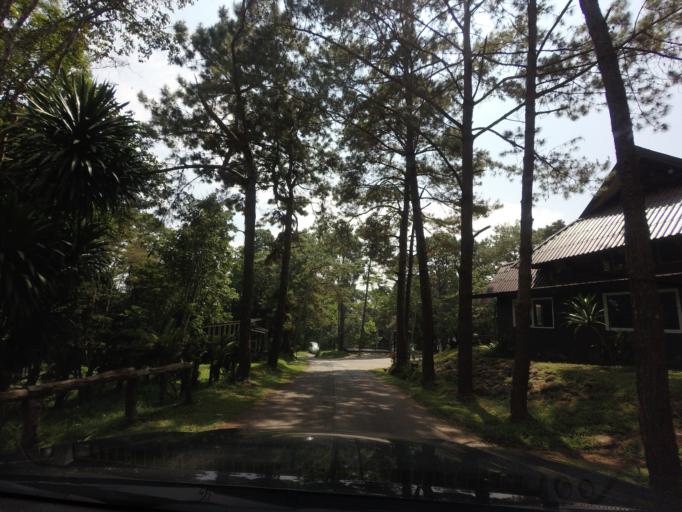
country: TH
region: Loei
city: Phu Ruea
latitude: 17.4817
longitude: 101.3521
